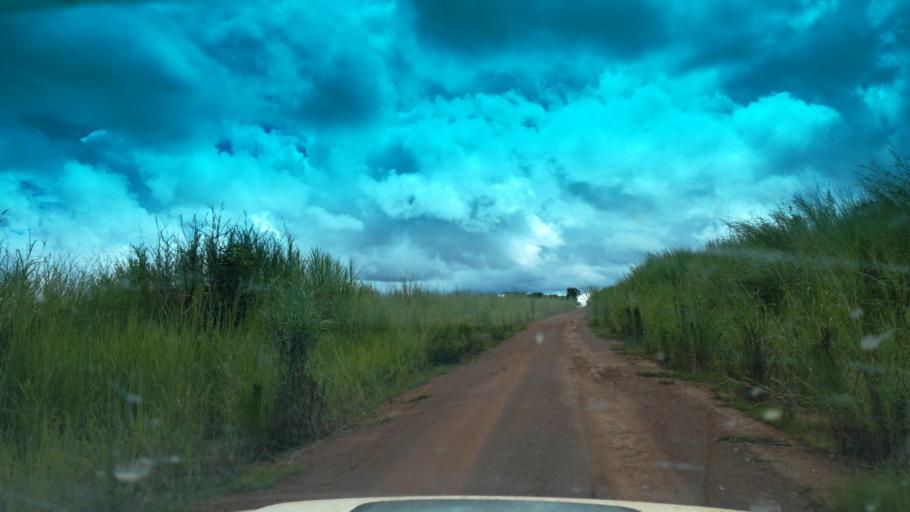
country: ZM
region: Northern
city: Kaputa
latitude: -7.7488
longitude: 29.2407
